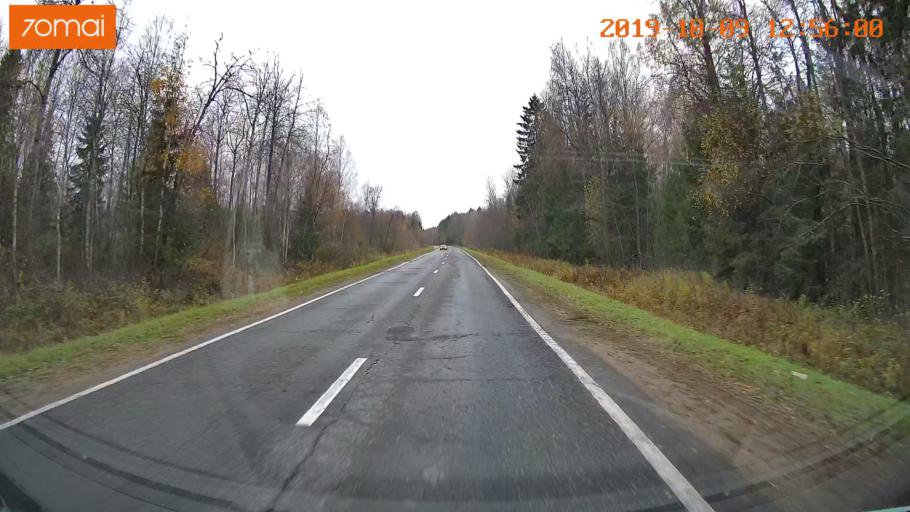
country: RU
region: Jaroslavl
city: Prechistoye
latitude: 58.3963
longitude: 40.4075
